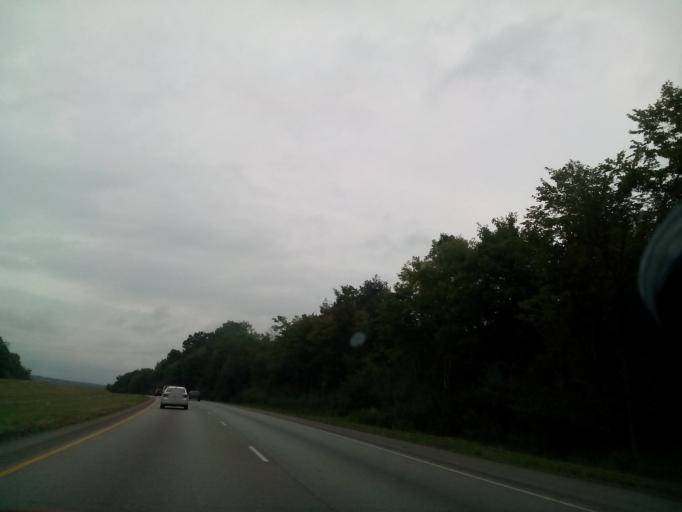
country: US
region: Ohio
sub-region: Trumbull County
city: Masury
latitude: 41.1779
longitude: -80.5329
